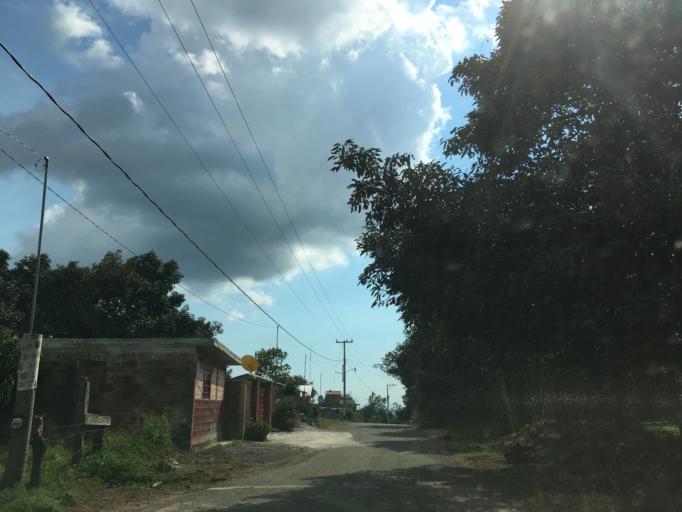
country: MX
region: Michoacan
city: Tingambato
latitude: 19.4429
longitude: -101.8694
